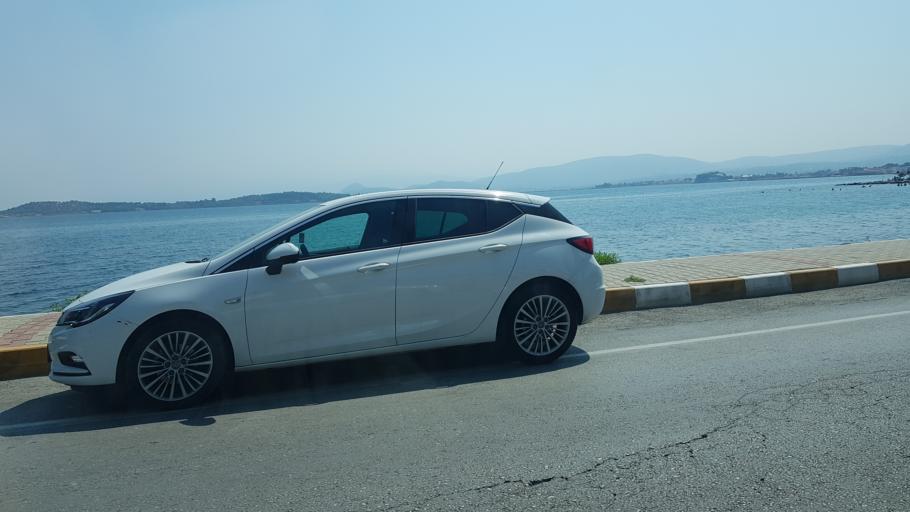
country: TR
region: Izmir
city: Urla
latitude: 38.3747
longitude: 26.7615
